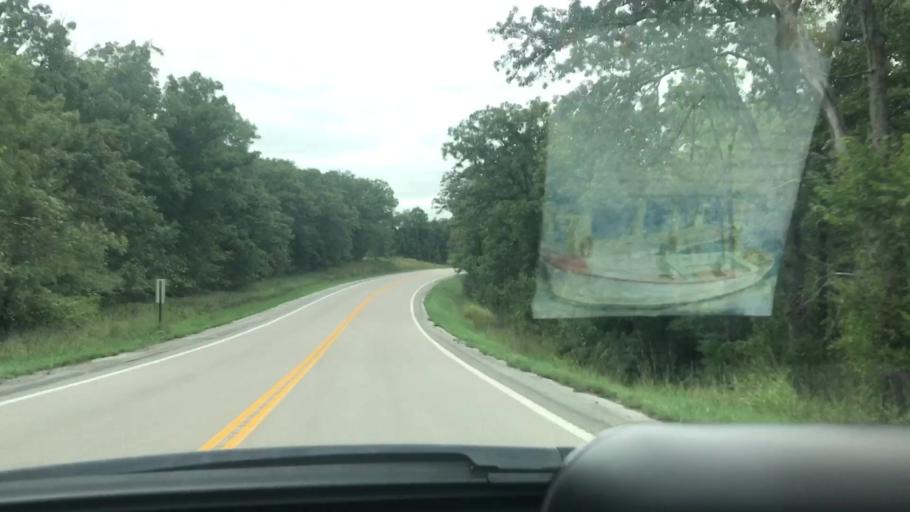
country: US
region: Missouri
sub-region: Benton County
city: Warsaw
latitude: 38.1625
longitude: -93.3026
